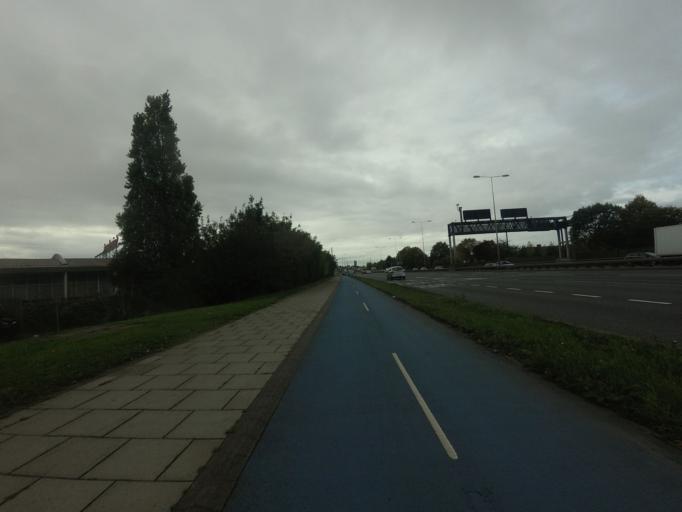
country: GB
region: England
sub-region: Greater London
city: East Ham
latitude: 51.5224
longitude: 0.0654
